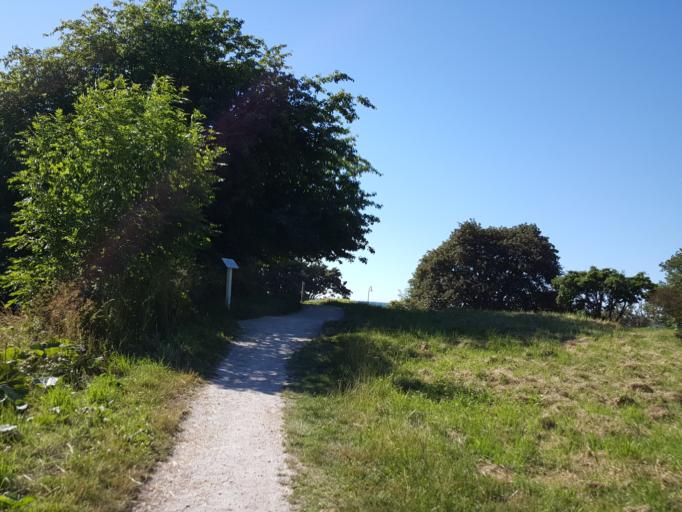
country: SE
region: Gotland
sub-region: Gotland
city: Visby
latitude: 57.6467
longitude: 18.2972
